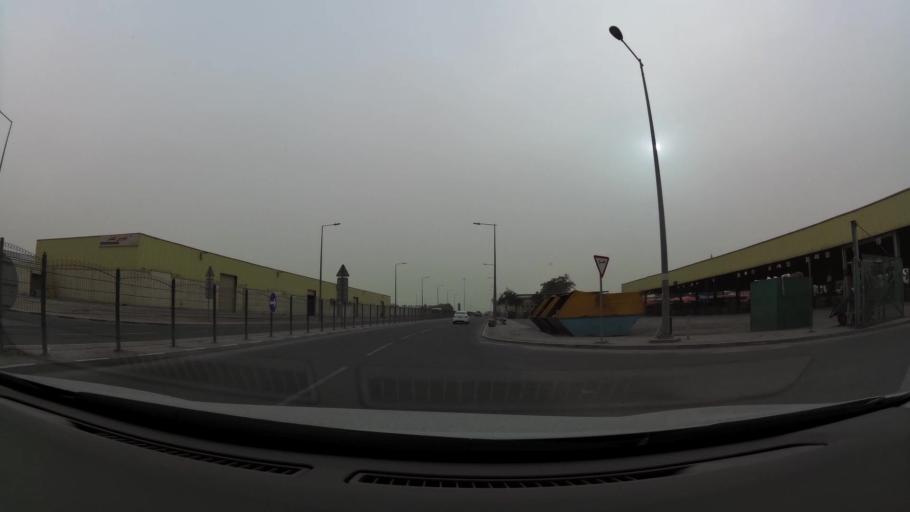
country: QA
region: Baladiyat ad Dawhah
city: Doha
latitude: 25.2459
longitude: 51.4782
